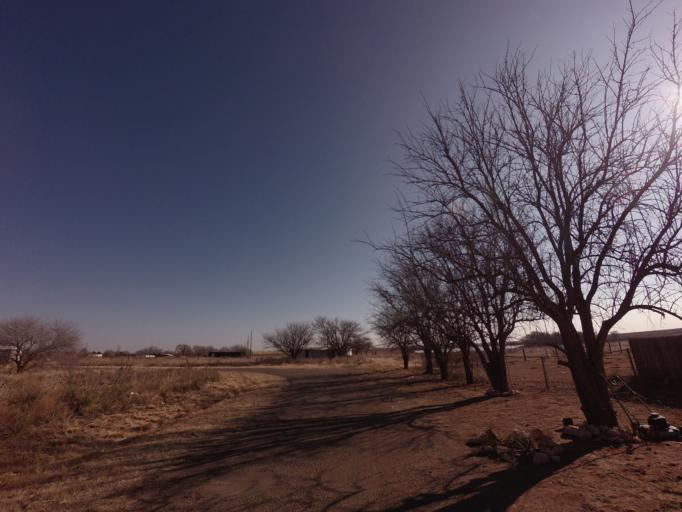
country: US
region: New Mexico
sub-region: Curry County
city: Clovis
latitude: 34.3834
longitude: -103.1840
